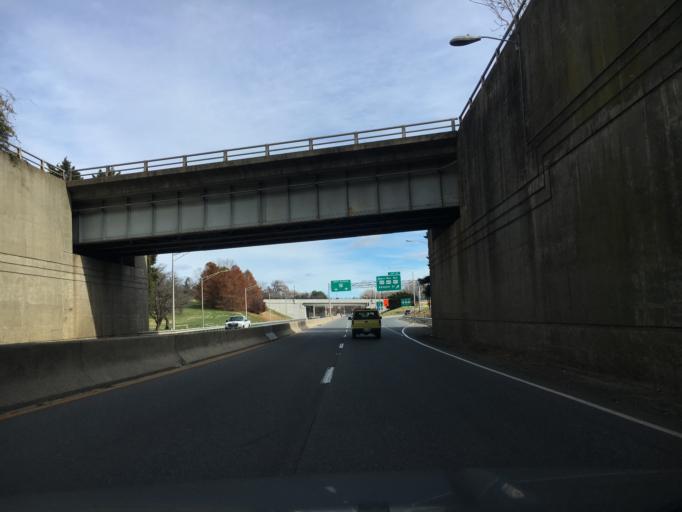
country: US
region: Virginia
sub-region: City of Lynchburg
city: Lynchburg
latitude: 37.3987
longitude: -79.1537
